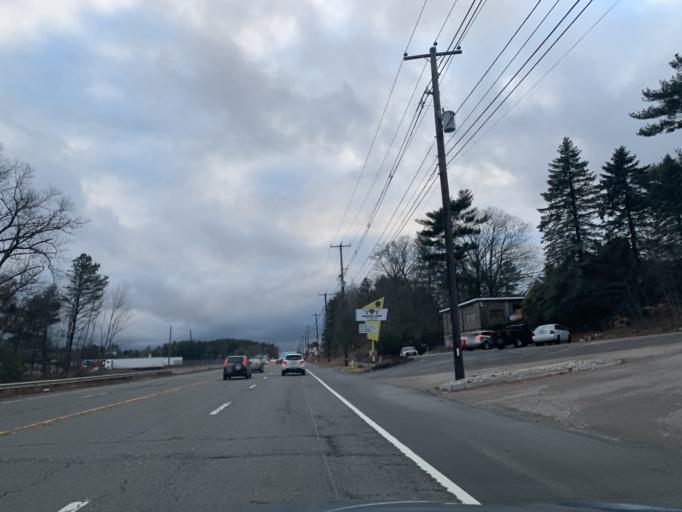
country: US
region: Massachusetts
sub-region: Norfolk County
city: Wrentham
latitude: 42.0501
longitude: -71.3009
